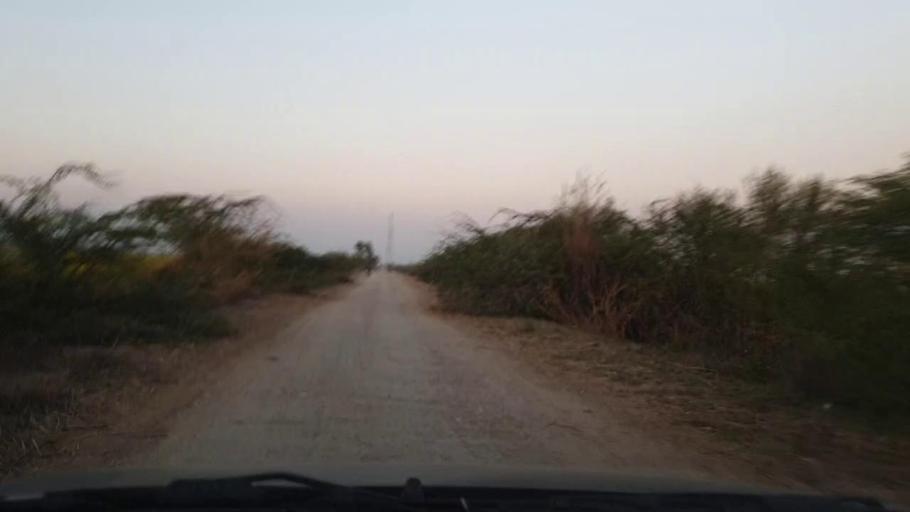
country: PK
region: Sindh
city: Jhol
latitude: 25.9469
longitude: 68.9749
